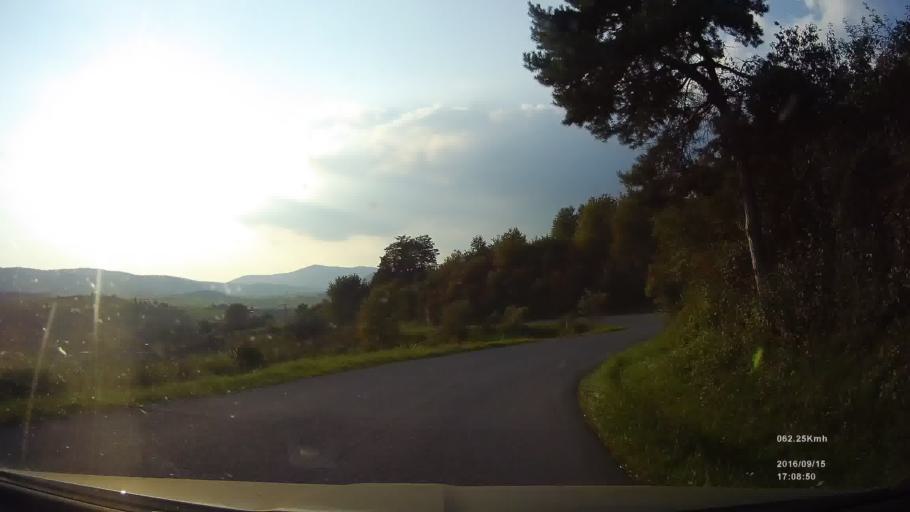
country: SK
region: Presovsky
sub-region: Okres Presov
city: Presov
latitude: 48.9154
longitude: 21.1300
